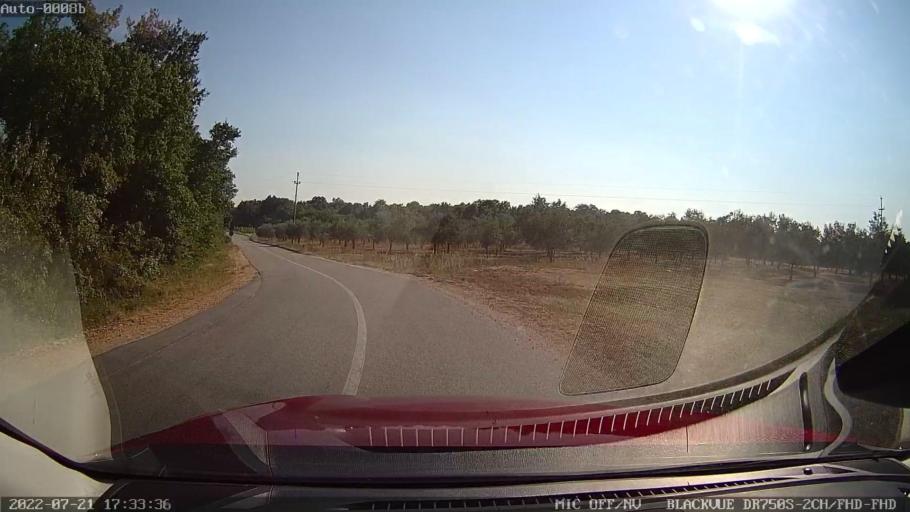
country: HR
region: Istarska
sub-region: Grad Rovinj
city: Rovinj
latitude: 45.1710
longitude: 13.7463
